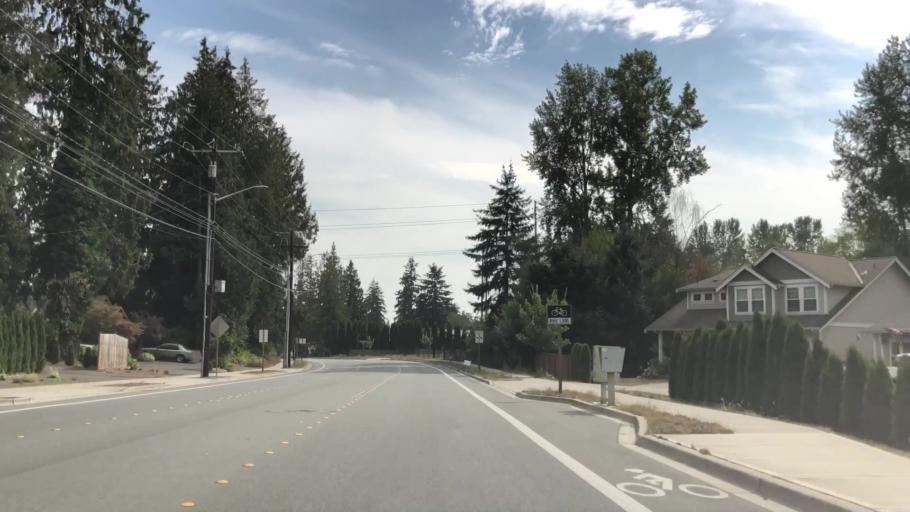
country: US
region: Washington
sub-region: Snohomish County
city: Martha Lake
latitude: 47.8309
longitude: -122.2378
